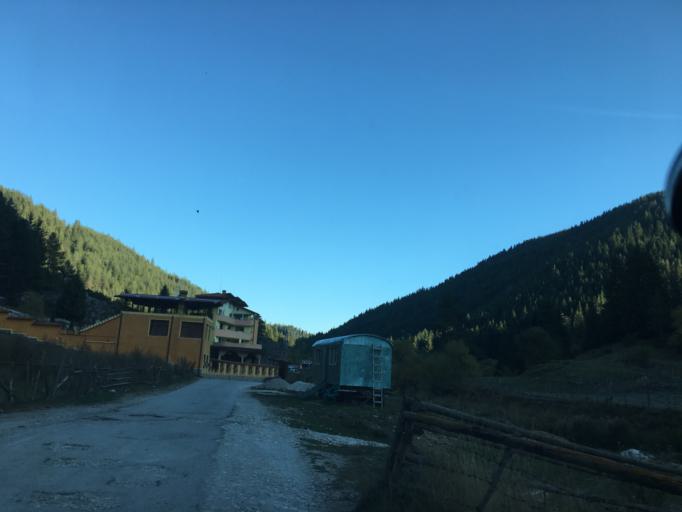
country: BG
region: Smolyan
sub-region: Obshtina Borino
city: Borino
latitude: 41.5847
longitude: 24.3918
